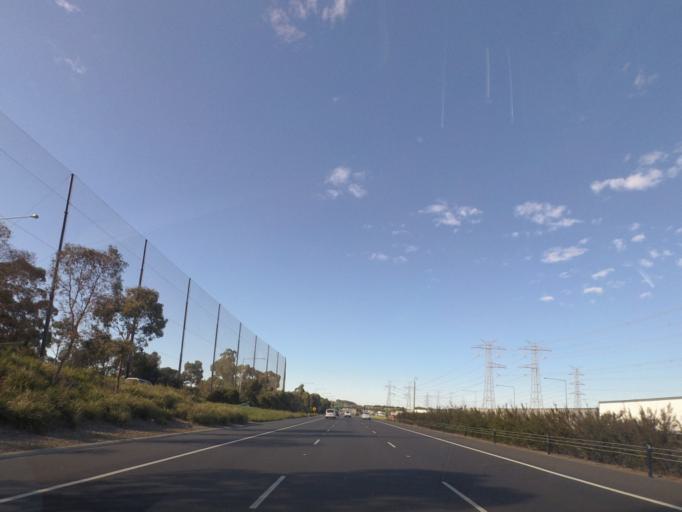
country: AU
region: Victoria
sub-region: Knox
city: Wantirna
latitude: -37.8343
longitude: 145.2177
